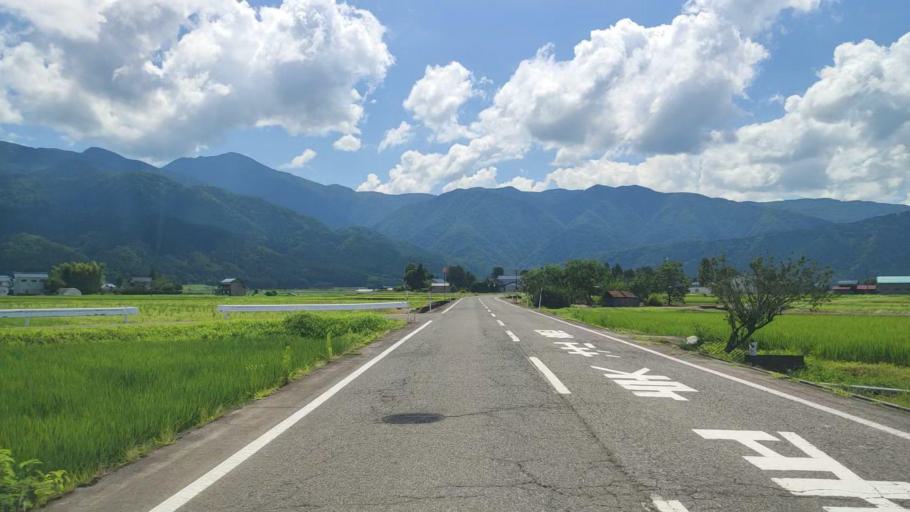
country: JP
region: Fukui
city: Ono
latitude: 35.9589
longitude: 136.5345
